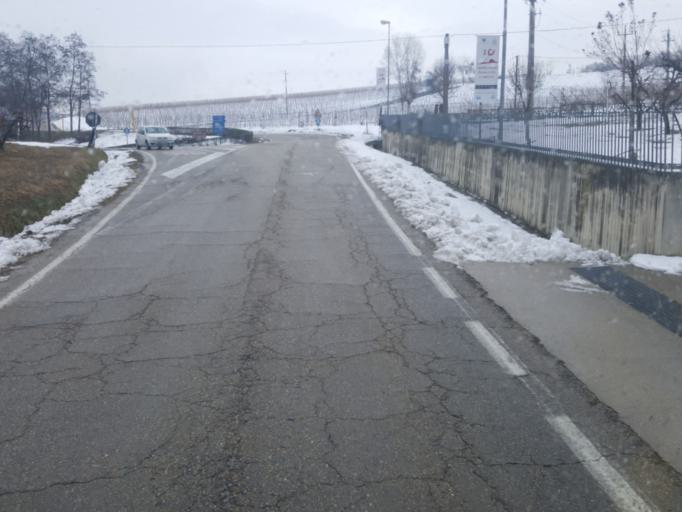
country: IT
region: Piedmont
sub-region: Provincia di Cuneo
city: Castagnito
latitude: 44.7639
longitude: 8.0291
